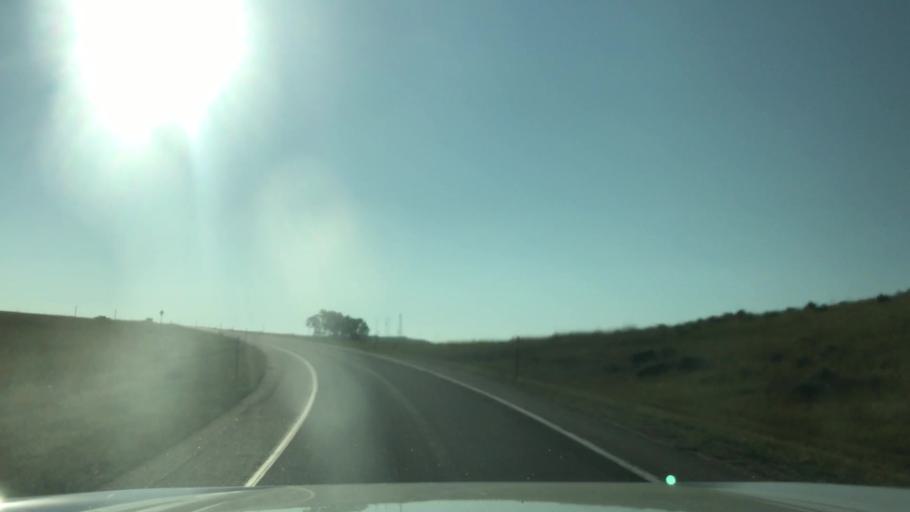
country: US
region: Wyoming
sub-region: Converse County
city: Douglas
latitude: 42.7295
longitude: -105.3392
